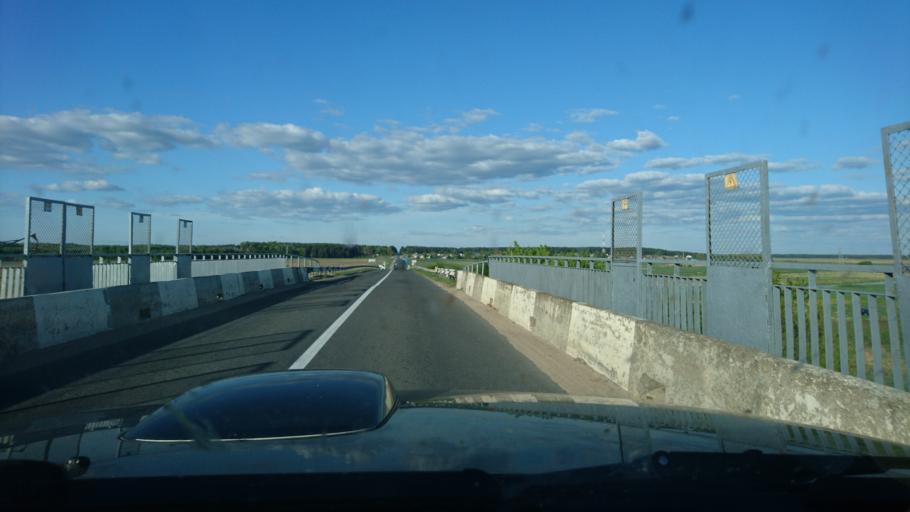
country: BY
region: Brest
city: Ivatsevichy
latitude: 52.7192
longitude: 25.3579
